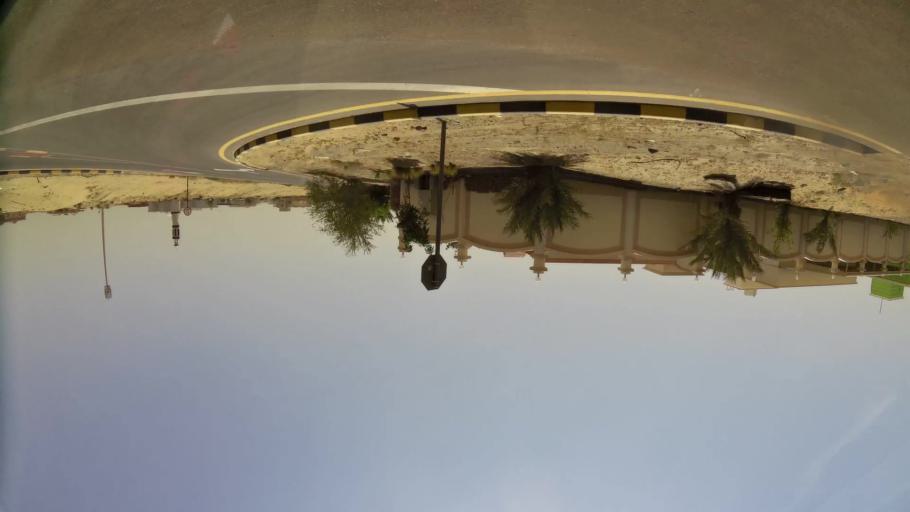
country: AE
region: Ajman
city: Ajman
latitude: 25.4182
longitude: 55.5242
